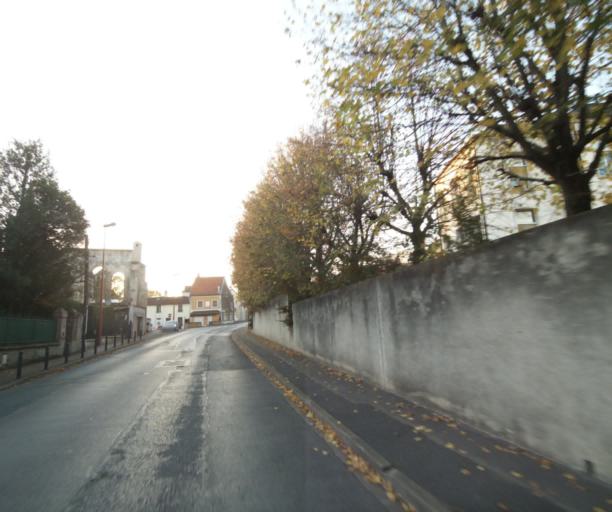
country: FR
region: Ile-de-France
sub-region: Departement du Val-d'Oise
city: Gonesse
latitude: 48.9887
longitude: 2.4487
